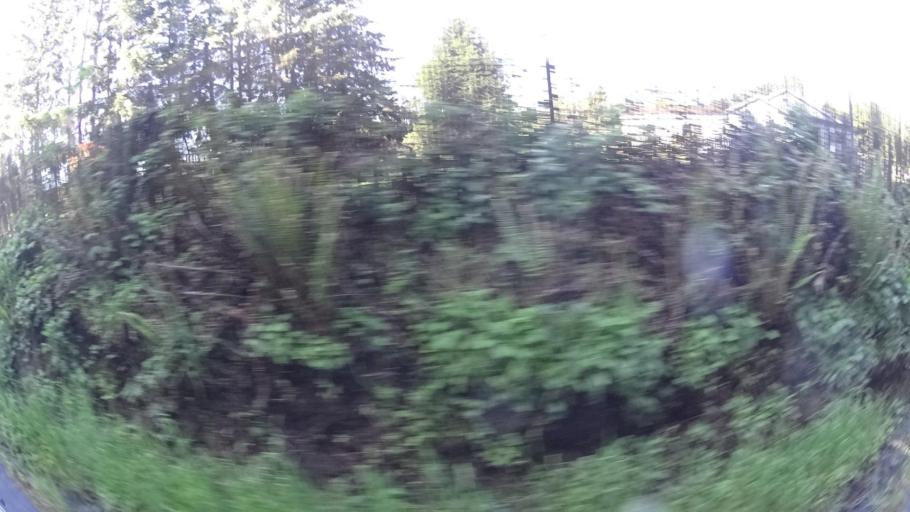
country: US
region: California
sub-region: Humboldt County
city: McKinleyville
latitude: 40.9801
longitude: -124.0963
